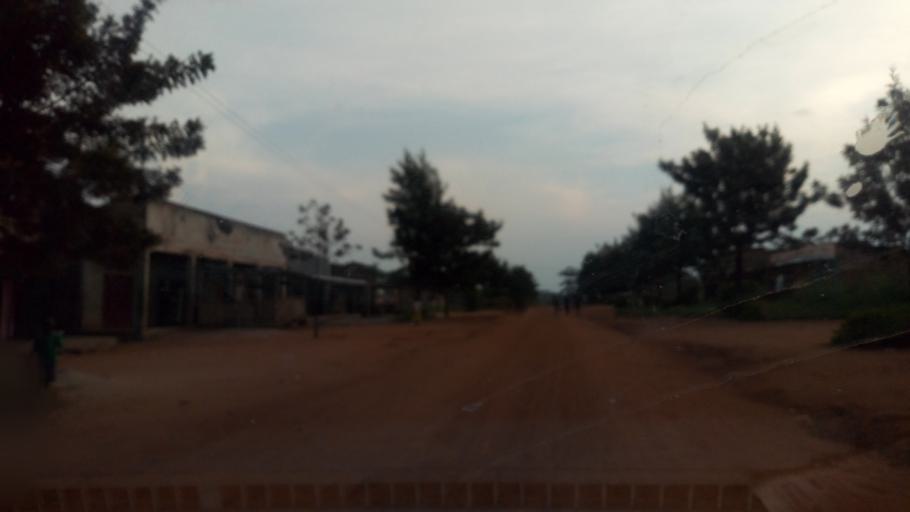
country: UG
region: Western Region
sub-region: Kiryandongo District
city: Kiryandongo
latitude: 1.8100
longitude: 32.0073
